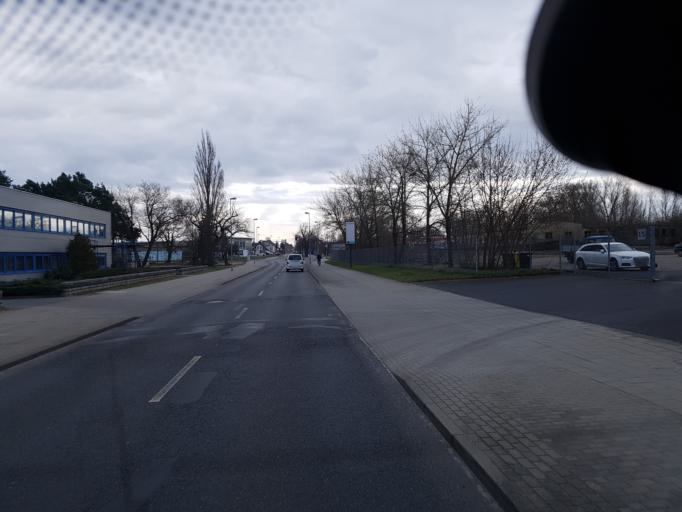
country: DE
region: Brandenburg
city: Eisenhuettenstadt
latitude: 52.1487
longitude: 14.6495
